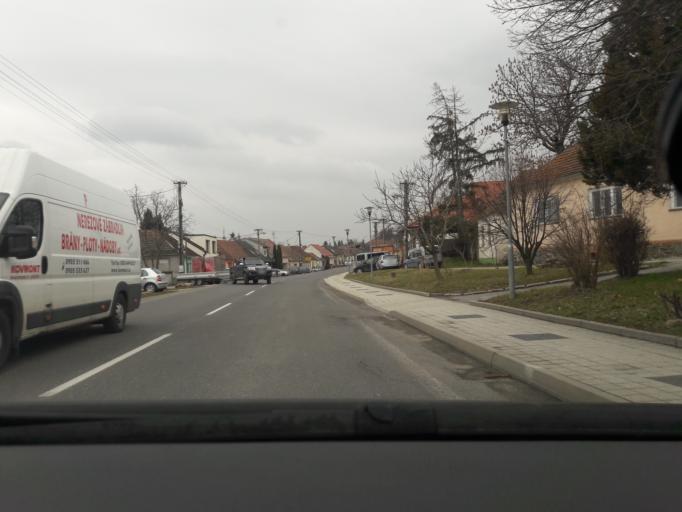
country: SK
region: Bratislavsky
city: Modra
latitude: 48.3968
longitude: 17.3559
